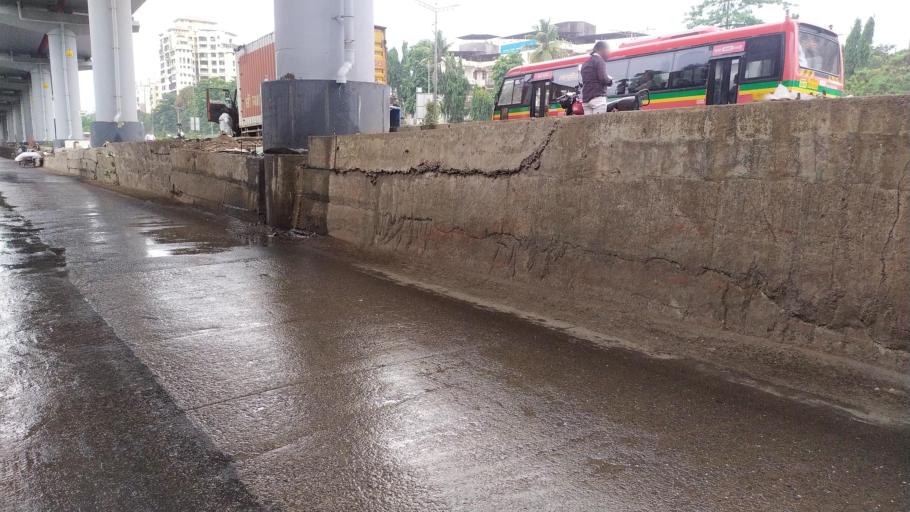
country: IN
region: Maharashtra
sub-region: Mumbai Suburban
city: Borivli
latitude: 19.2364
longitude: 72.8630
